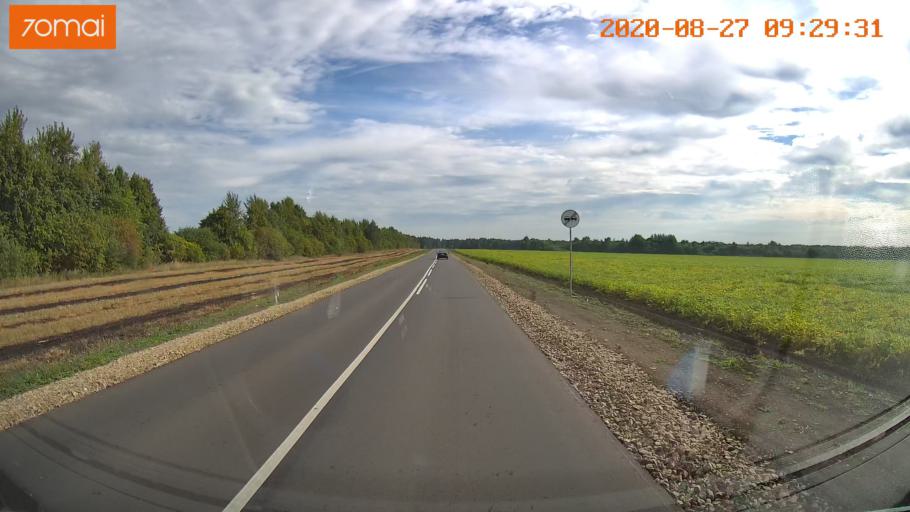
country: RU
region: Tula
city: Kazachka
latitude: 53.3149
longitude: 38.2240
